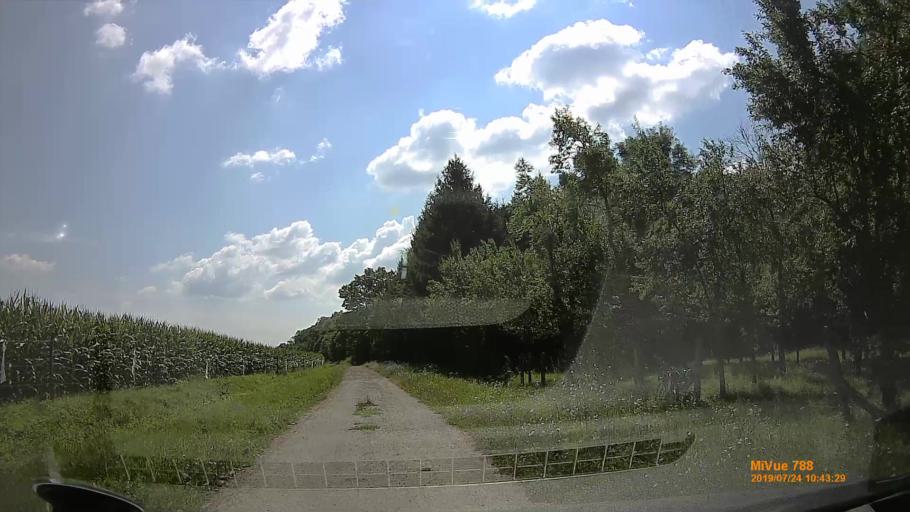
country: UA
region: Zakarpattia
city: Berehove
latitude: 48.1968
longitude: 22.5558
